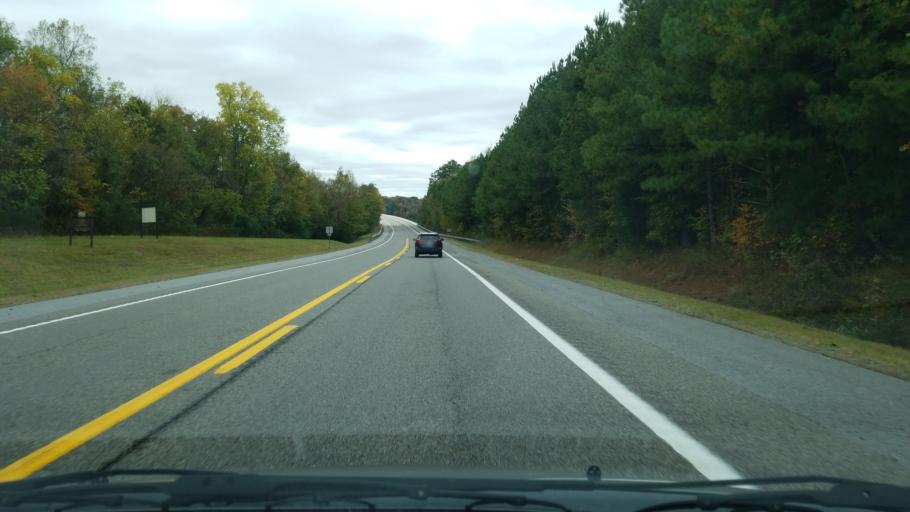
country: US
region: Tennessee
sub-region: Rhea County
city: Graysville
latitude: 35.4168
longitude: -85.0231
